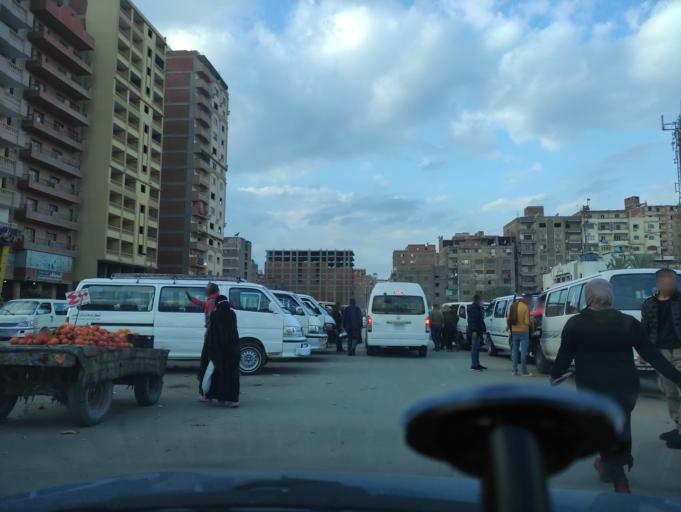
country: EG
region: Muhafazat al Qalyubiyah
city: Al Khankah
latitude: 30.1288
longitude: 31.3619
